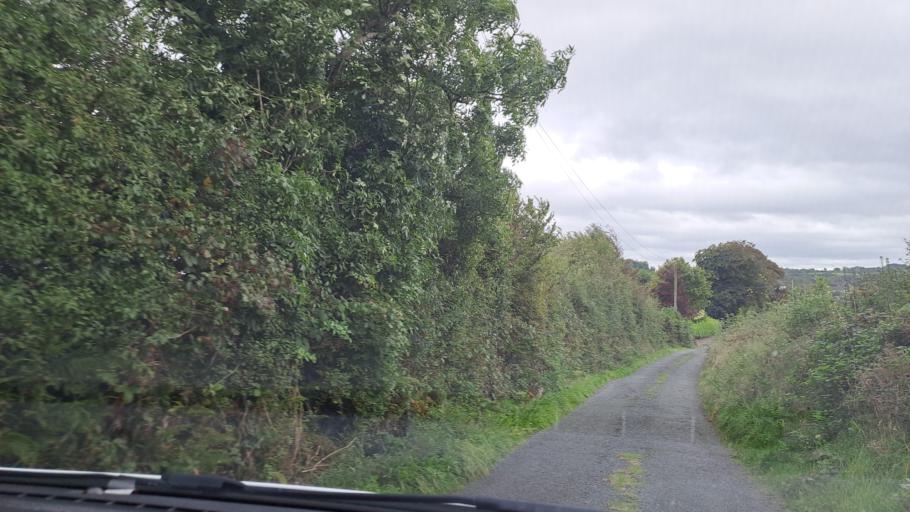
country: IE
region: Ulster
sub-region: An Cabhan
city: Bailieborough
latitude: 54.0000
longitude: -6.9003
